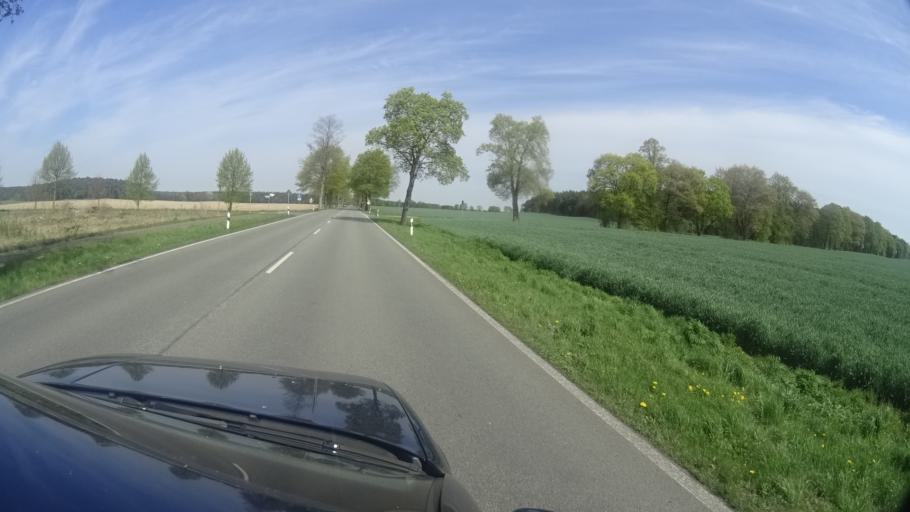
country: DE
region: Brandenburg
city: Friesack
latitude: 52.7079
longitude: 12.5969
